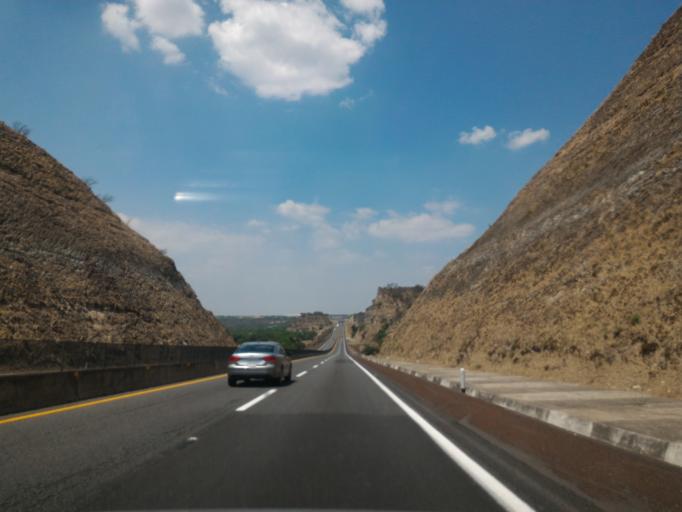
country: MX
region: Jalisco
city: Jalostotitlan
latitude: 21.1450
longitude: -102.4299
